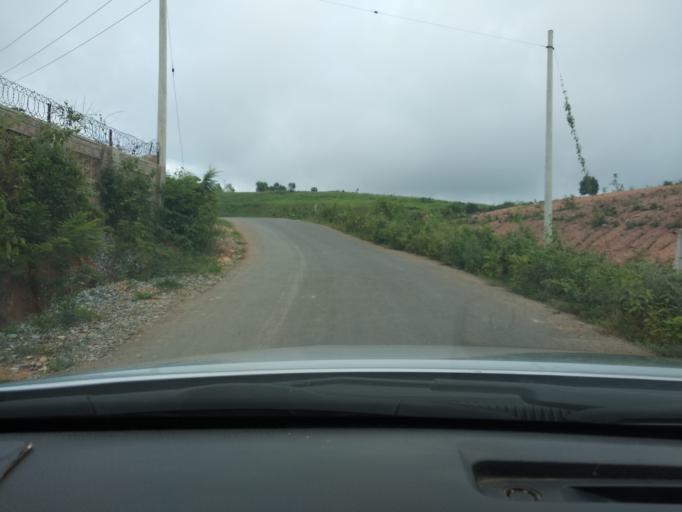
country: MM
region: Mandalay
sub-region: Pyin Oo Lwin District
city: Pyin Oo Lwin
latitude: 21.9190
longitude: 96.3820
